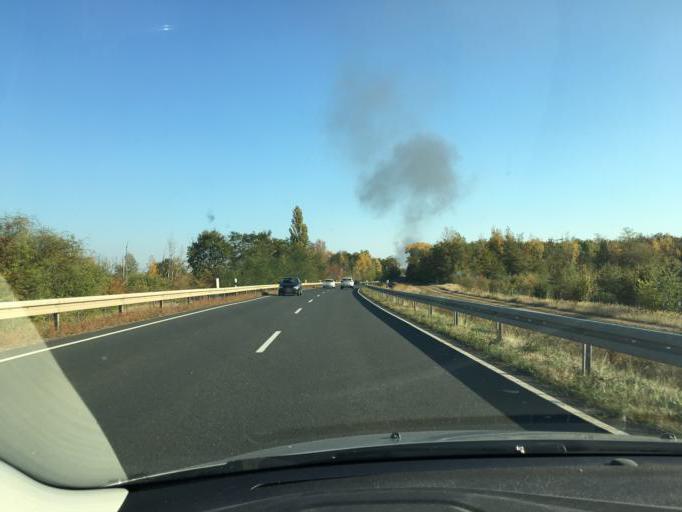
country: DE
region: Saxony-Anhalt
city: Sandersdorf
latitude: 51.6428
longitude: 12.2644
